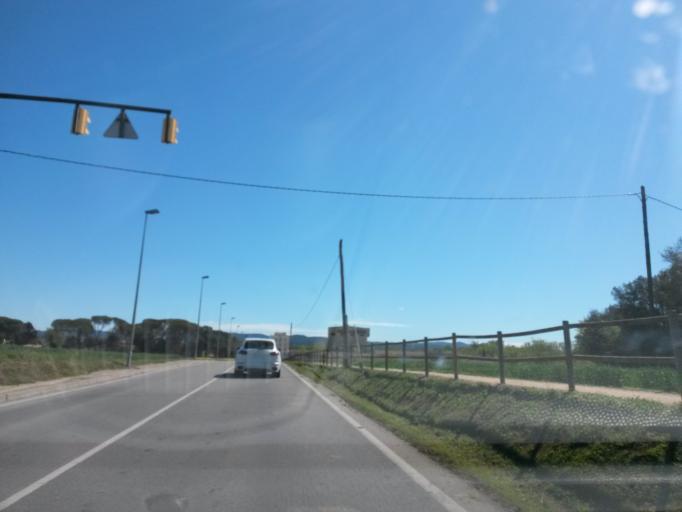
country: ES
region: Catalonia
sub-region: Provincia de Girona
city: Riudellots de la Selva
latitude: 41.8949
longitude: 2.8063
